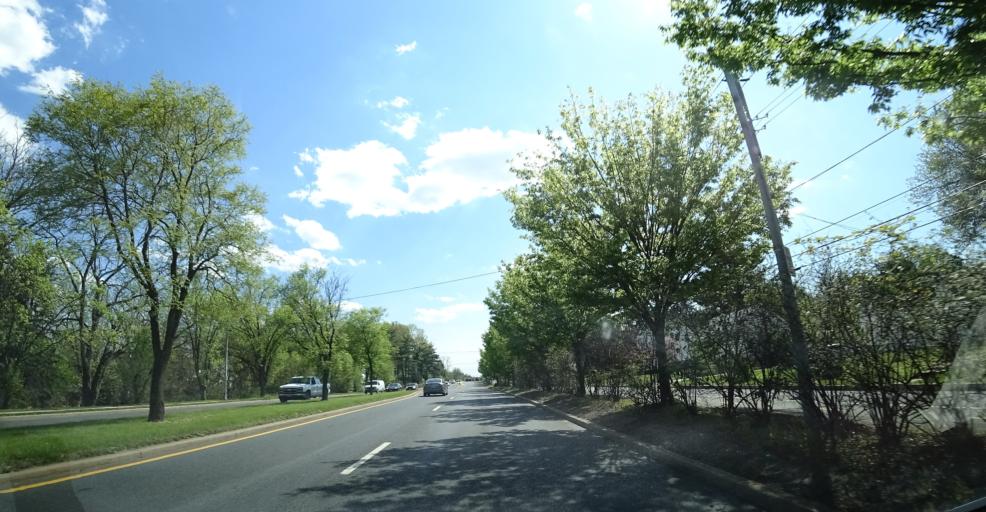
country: US
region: Maryland
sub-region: Montgomery County
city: Rockville
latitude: 39.0834
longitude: -77.1368
